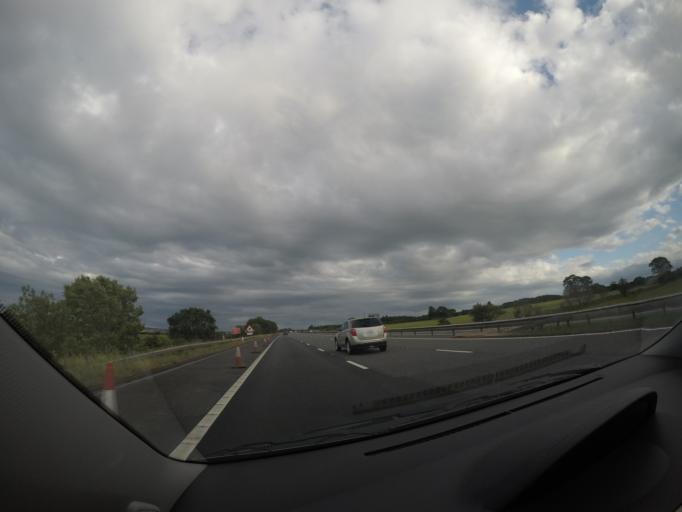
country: GB
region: England
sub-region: Cumbria
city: Scotby
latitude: 54.7881
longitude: -2.8627
